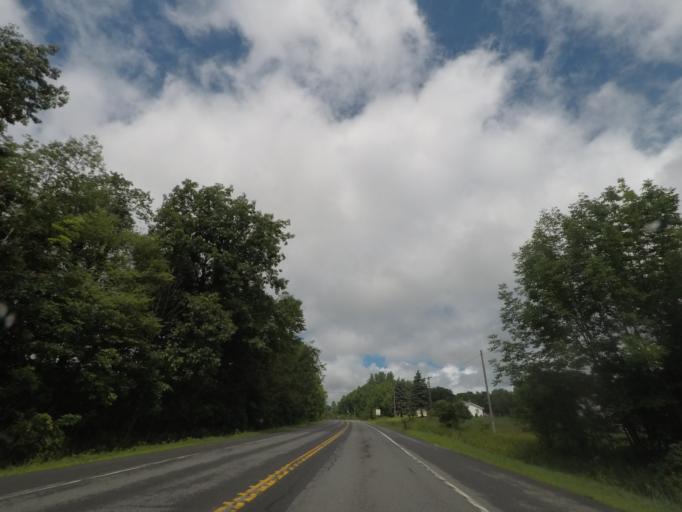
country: US
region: Massachusetts
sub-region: Berkshire County
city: Lanesborough
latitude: 42.5979
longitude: -73.3694
